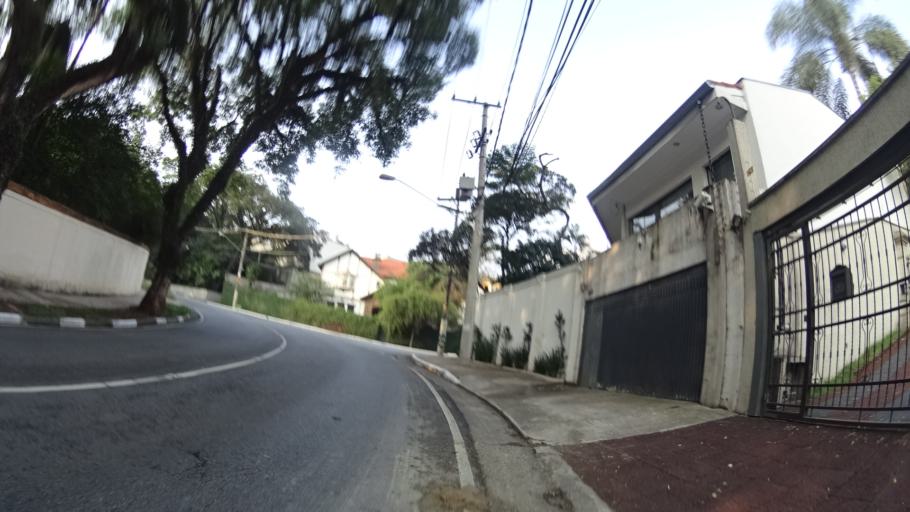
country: BR
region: Sao Paulo
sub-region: Sao Paulo
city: Sao Paulo
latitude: -23.5502
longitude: -46.6637
